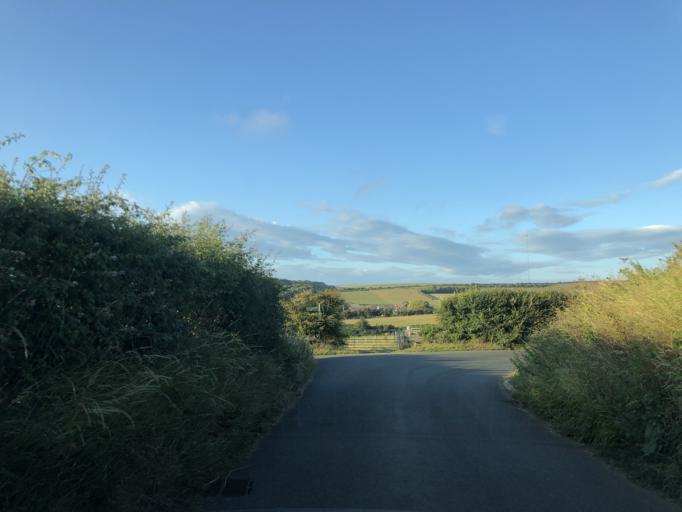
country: GB
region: England
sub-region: Isle of Wight
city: Chale
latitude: 50.6388
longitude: -1.3600
